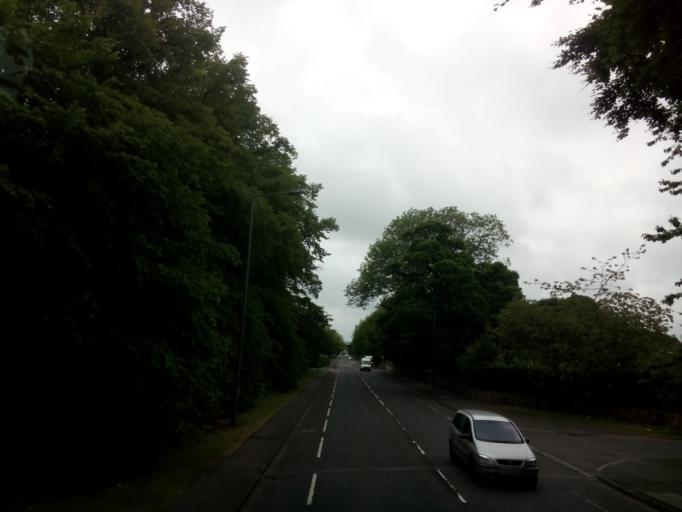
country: GB
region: England
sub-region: County Durham
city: Chester-le-Street
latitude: 54.8717
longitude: -1.5752
